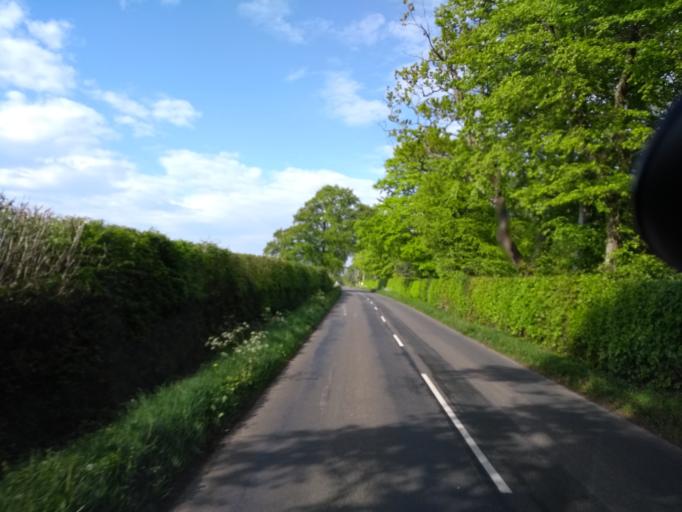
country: GB
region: England
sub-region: Dorset
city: Lyme Regis
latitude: 50.7802
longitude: -2.9357
